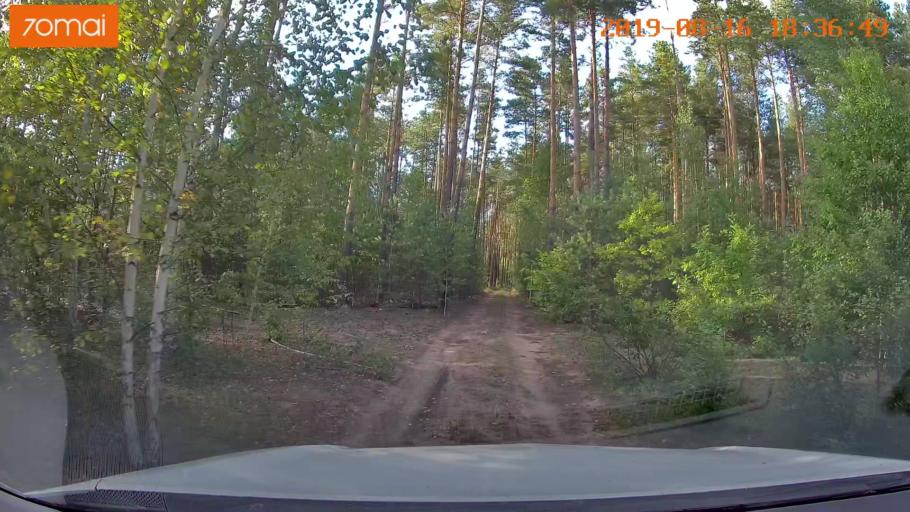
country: BY
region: Mogilev
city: Asipovichy
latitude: 53.2066
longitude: 28.6337
